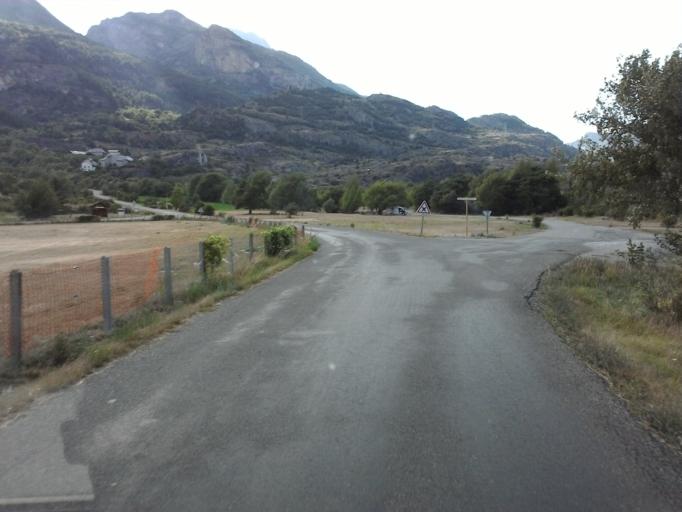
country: FR
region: Provence-Alpes-Cote d'Azur
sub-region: Departement des Hautes-Alpes
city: Guillestre
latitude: 44.7063
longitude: 6.5974
